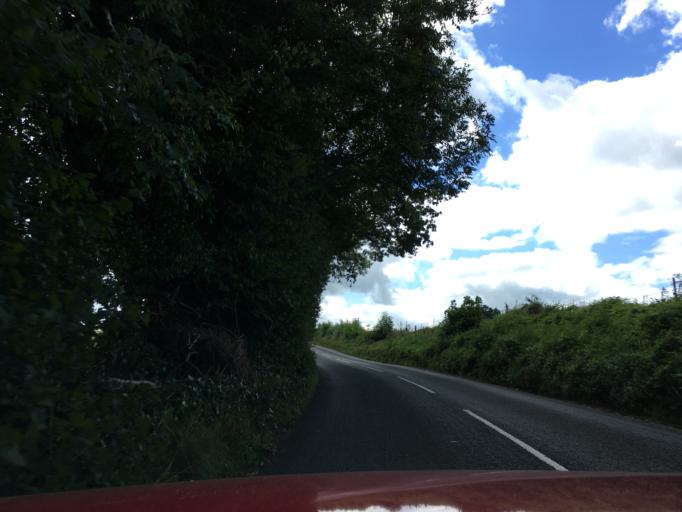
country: GB
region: England
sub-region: Wiltshire
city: Colerne
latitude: 51.4690
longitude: -2.2435
